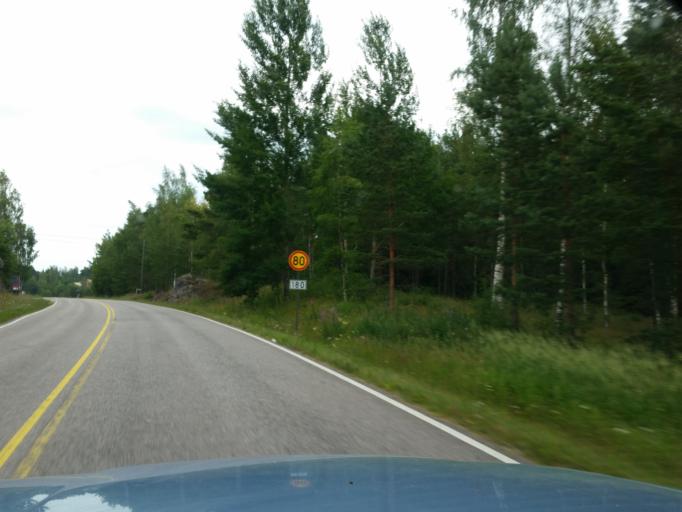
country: FI
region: Varsinais-Suomi
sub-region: Aboland-Turunmaa
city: Nagu
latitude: 60.1806
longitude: 21.9730
